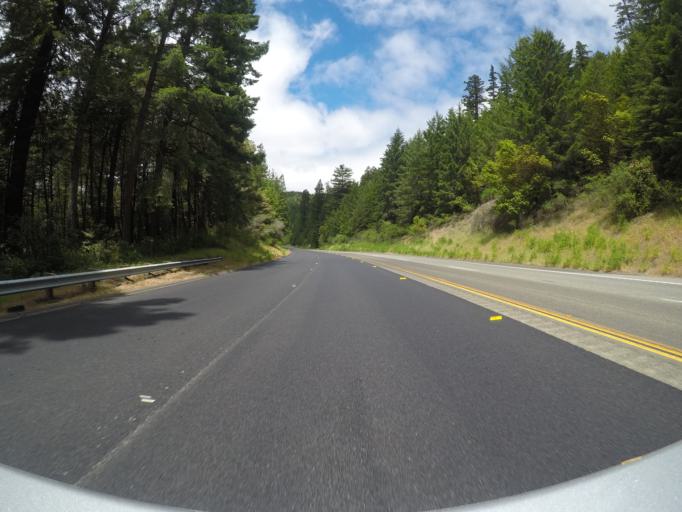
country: US
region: California
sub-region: Humboldt County
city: Redway
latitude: 40.2987
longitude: -123.8921
